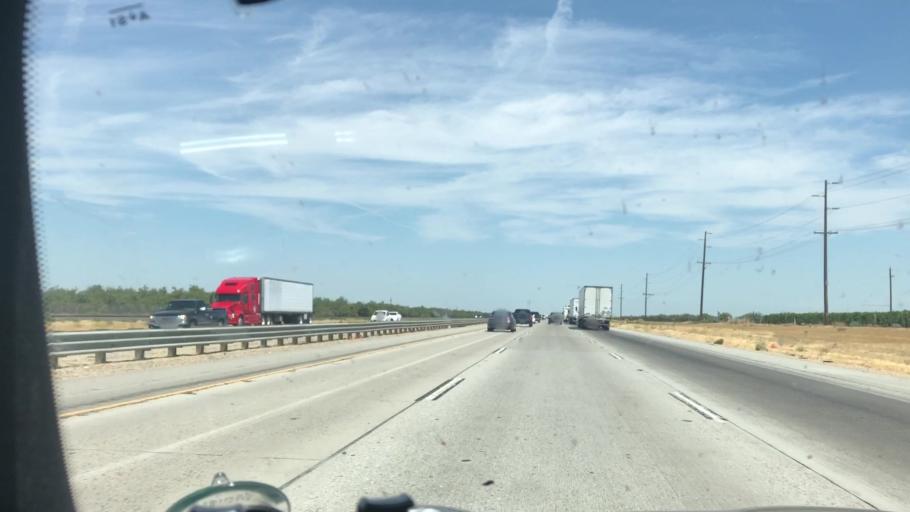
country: US
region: California
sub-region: Kern County
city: Shafter
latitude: 35.5715
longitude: -119.2012
